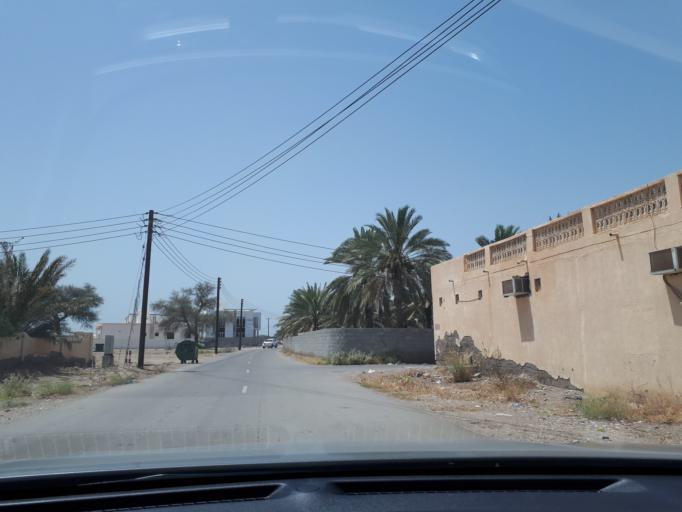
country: OM
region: Muhafazat Masqat
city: As Sib al Jadidah
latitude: 23.6907
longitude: 58.1086
